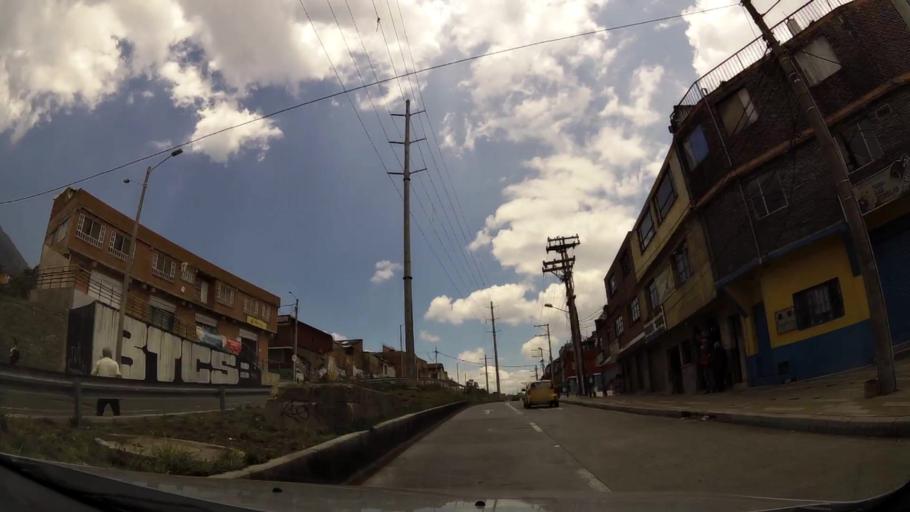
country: CO
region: Bogota D.C.
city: Bogota
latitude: 4.5915
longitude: -74.0706
